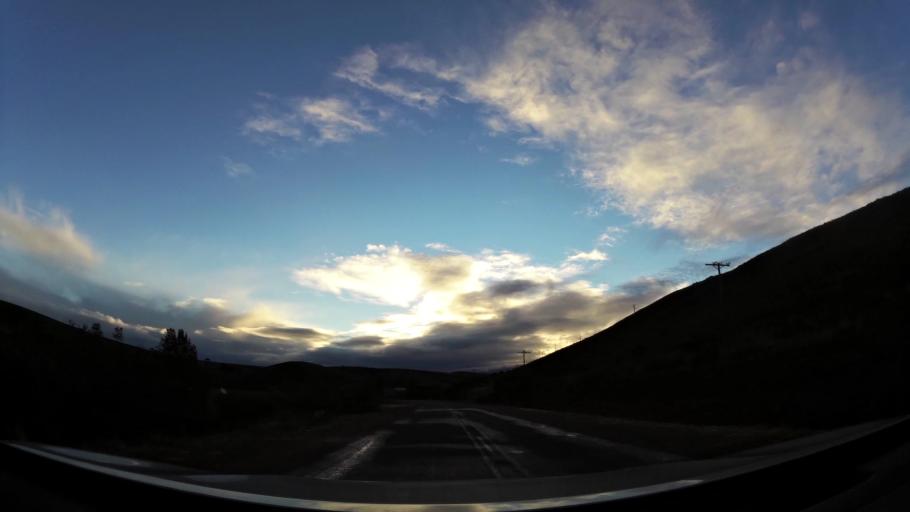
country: ZA
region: Western Cape
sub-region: Eden District Municipality
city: Riversdale
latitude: -34.0556
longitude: 20.8612
